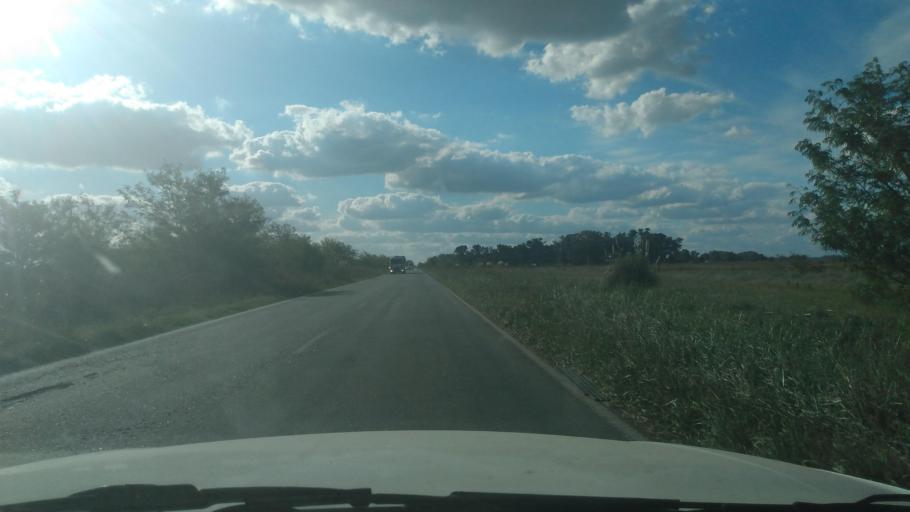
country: AR
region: Buenos Aires
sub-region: Partido de Mercedes
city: Mercedes
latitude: -34.7656
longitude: -59.3736
